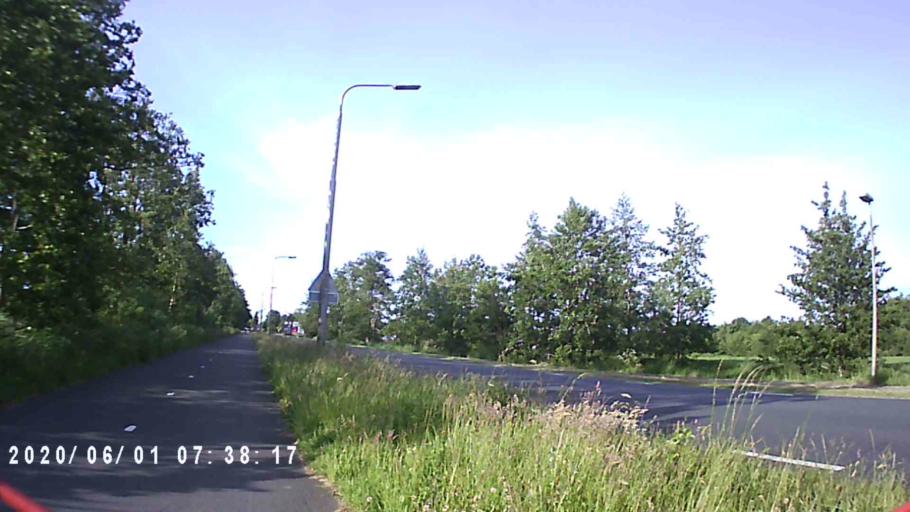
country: NL
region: Friesland
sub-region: Gemeente Dantumadiel
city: Damwald
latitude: 53.2960
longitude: 5.9968
